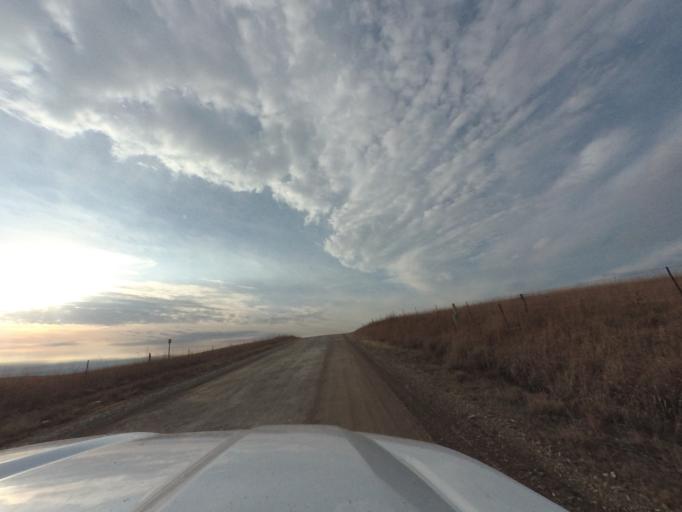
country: US
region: Kansas
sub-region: Morris County
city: Council Grove
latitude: 38.5127
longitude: -96.4099
